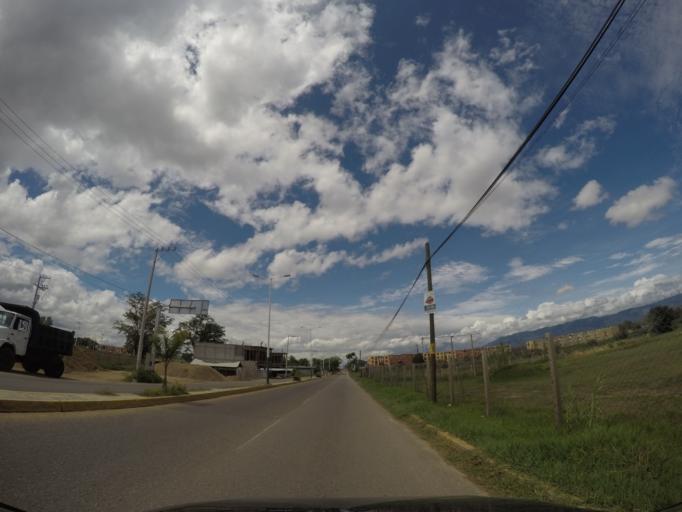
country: MX
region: Oaxaca
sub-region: Santa Cruz Xoxocotlan
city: Santa Cruz Xoxocotlan
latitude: 17.0164
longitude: -96.7331
